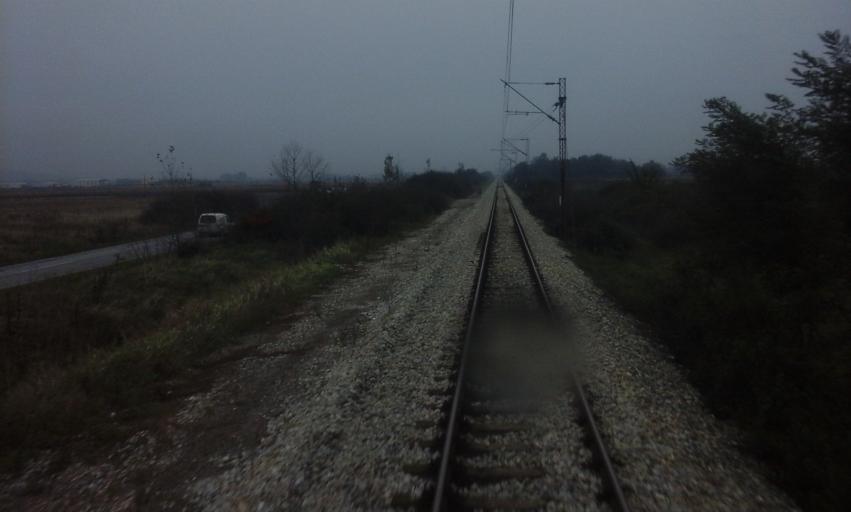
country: RS
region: Central Serbia
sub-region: Pomoravski Okrug
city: Cuprija
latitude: 43.8965
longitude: 21.3806
